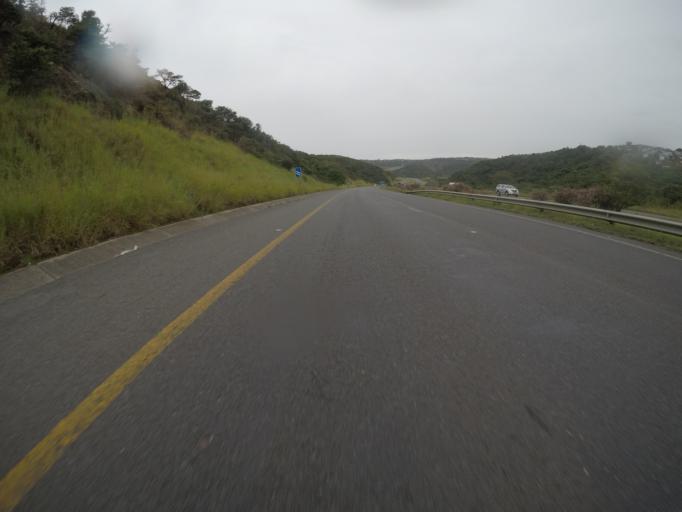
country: ZA
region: Eastern Cape
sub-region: Buffalo City Metropolitan Municipality
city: East London
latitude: -32.9595
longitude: 27.9270
